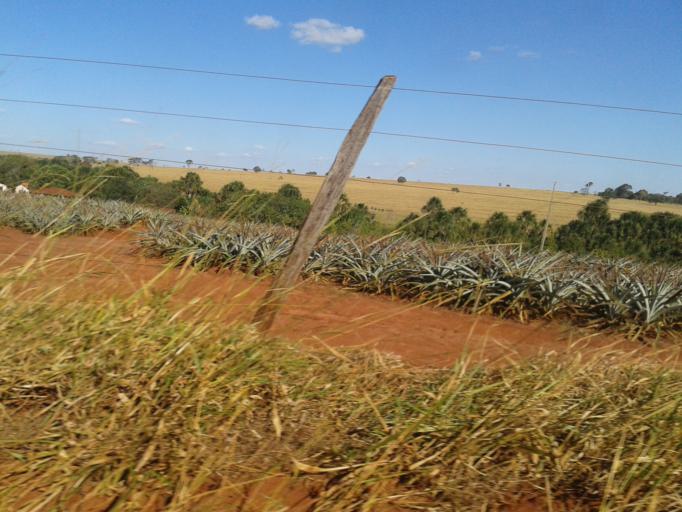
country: BR
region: Minas Gerais
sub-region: Centralina
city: Centralina
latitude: -18.7525
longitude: -49.1827
